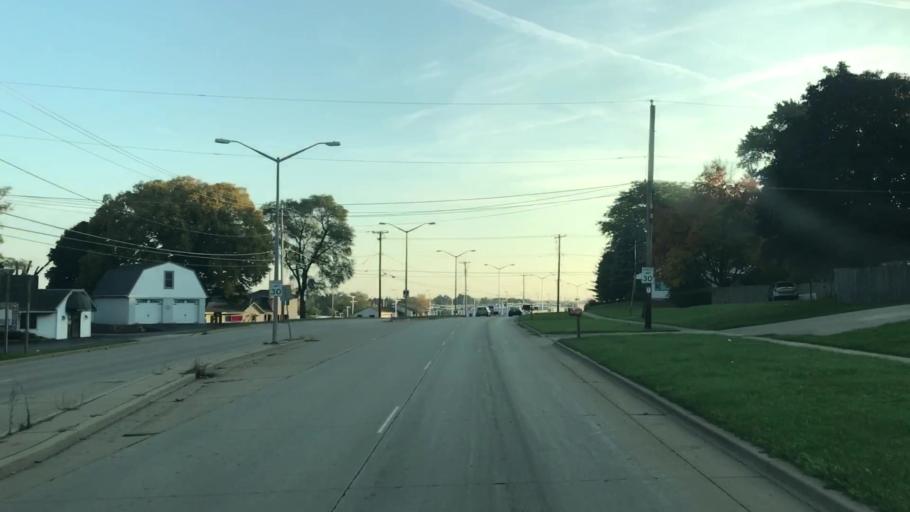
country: US
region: Wisconsin
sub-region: Waukesha County
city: Waukesha
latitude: 43.0238
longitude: -88.1946
